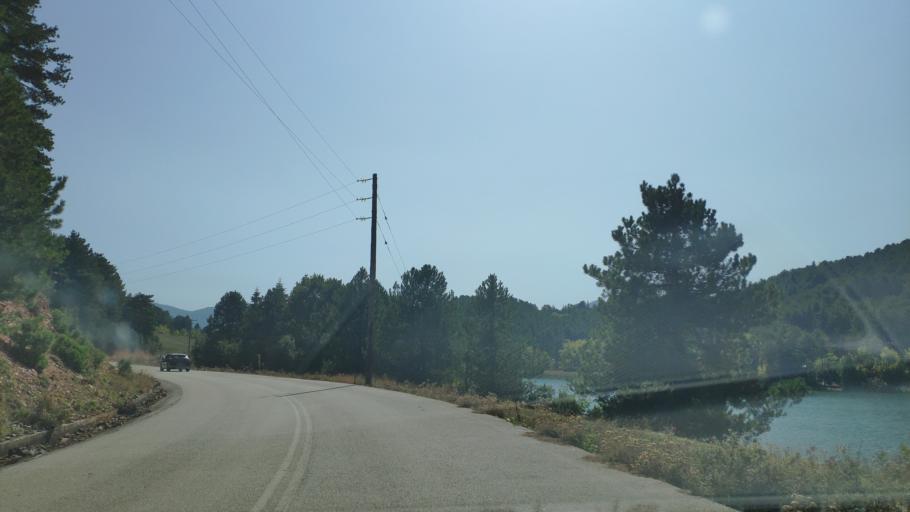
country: GR
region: West Greece
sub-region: Nomos Achaias
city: Kalavryta
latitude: 37.9276
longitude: 22.2913
